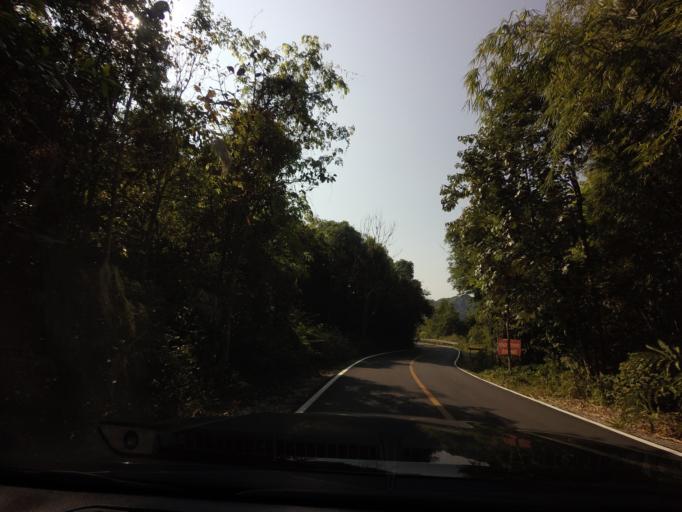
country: TH
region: Kanchanaburi
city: Thong Pha Phum
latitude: 14.6845
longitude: 98.4170
